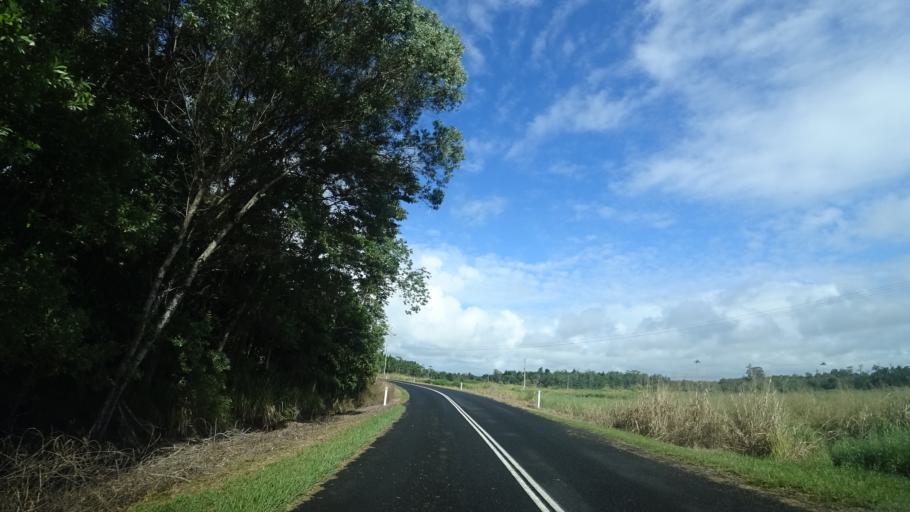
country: AU
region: Queensland
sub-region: Cassowary Coast
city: Innisfail
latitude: -17.5684
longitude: 146.0859
